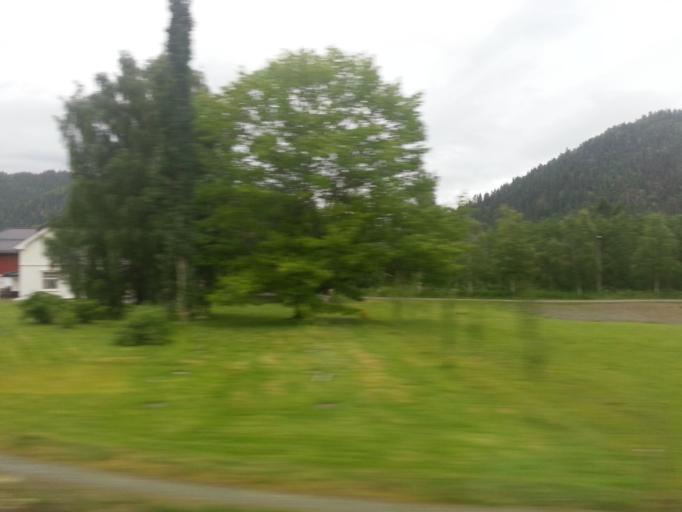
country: NO
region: Sor-Trondelag
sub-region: Melhus
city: Lundamo
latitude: 63.1537
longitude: 10.2839
